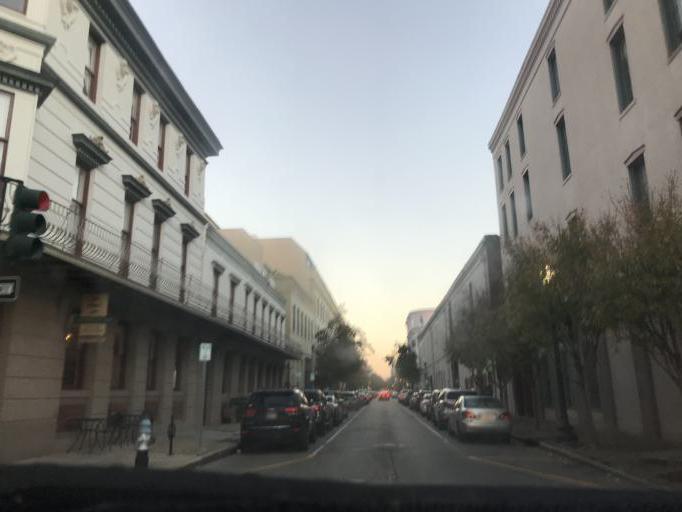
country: US
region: Louisiana
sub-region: Orleans Parish
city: New Orleans
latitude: 29.9471
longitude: -90.0701
